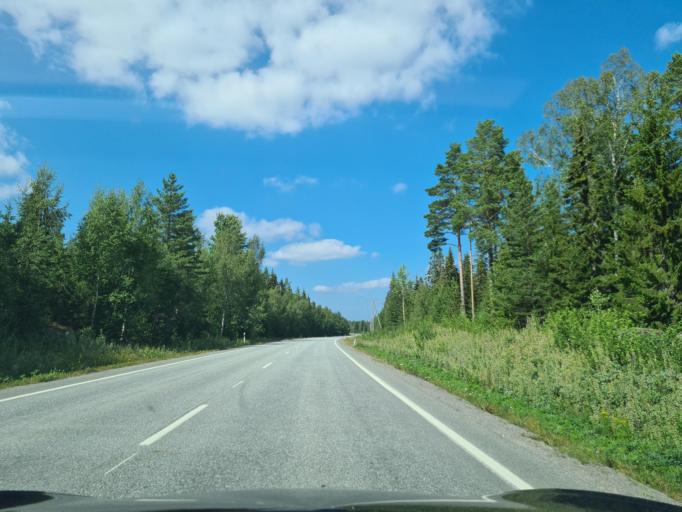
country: FI
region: Ostrobothnia
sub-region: Vaasa
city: Vaasa
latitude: 63.1734
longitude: 21.5795
